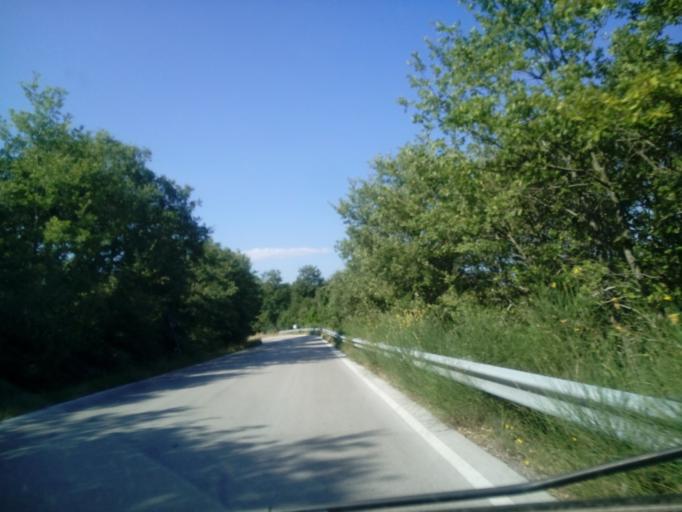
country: IT
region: Molise
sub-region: Provincia di Campobasso
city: Gildone
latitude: 41.5186
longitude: 14.7519
